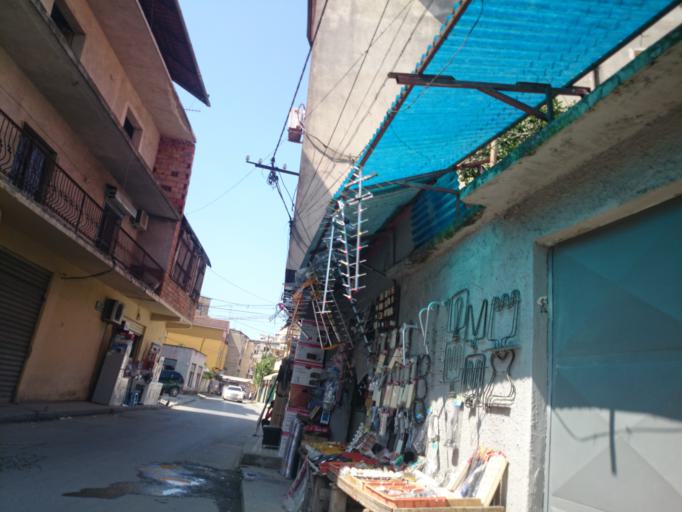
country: AL
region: Tirane
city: Tirana
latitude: 41.3262
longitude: 19.8318
